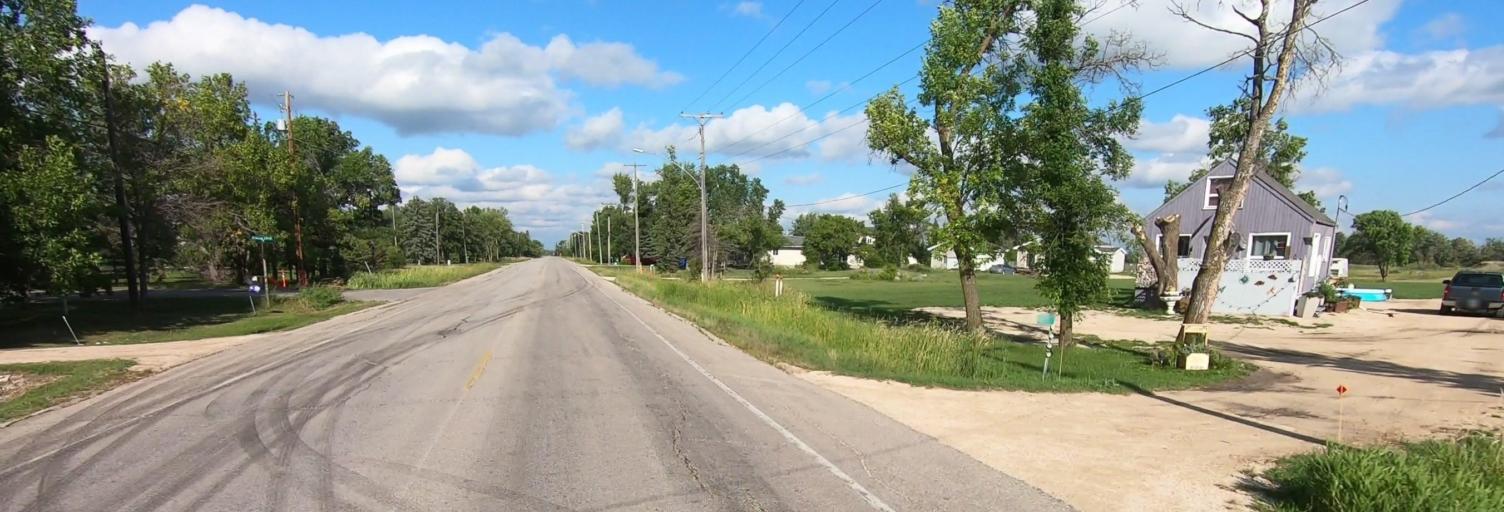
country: CA
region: Manitoba
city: Selkirk
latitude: 50.0340
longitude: -96.9970
